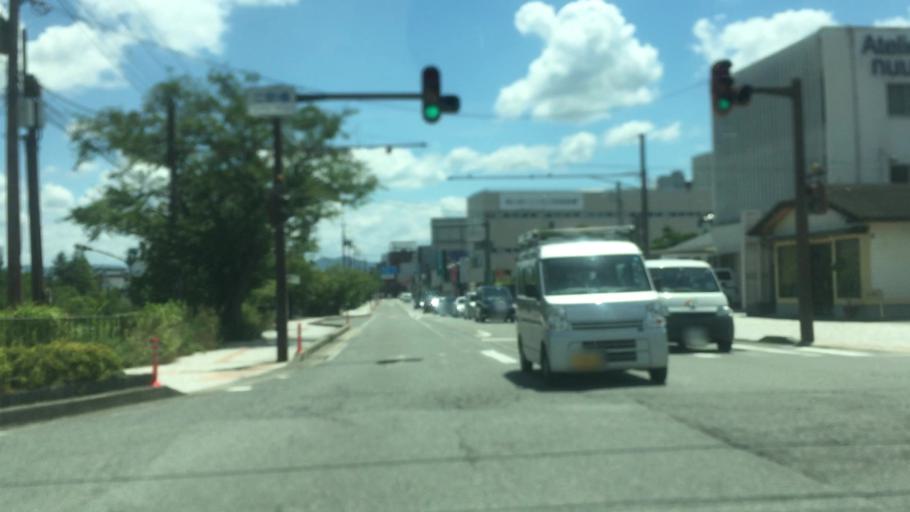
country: JP
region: Hyogo
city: Toyooka
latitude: 35.5437
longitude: 134.8248
